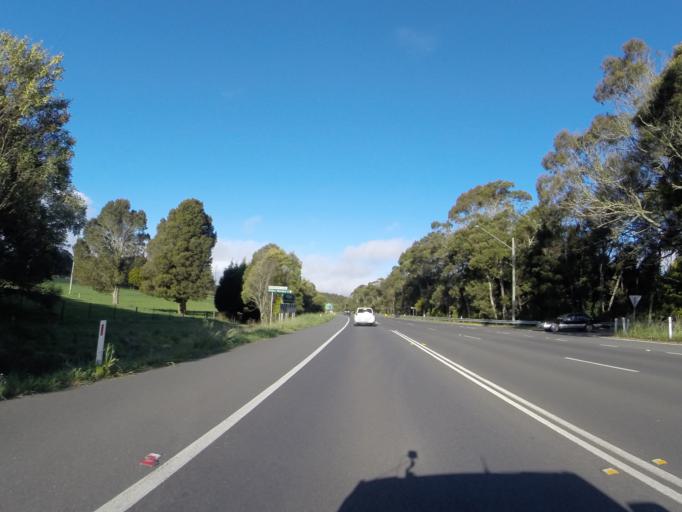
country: AU
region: New South Wales
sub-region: Shellharbour
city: Calderwood
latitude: -34.5897
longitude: 150.5698
